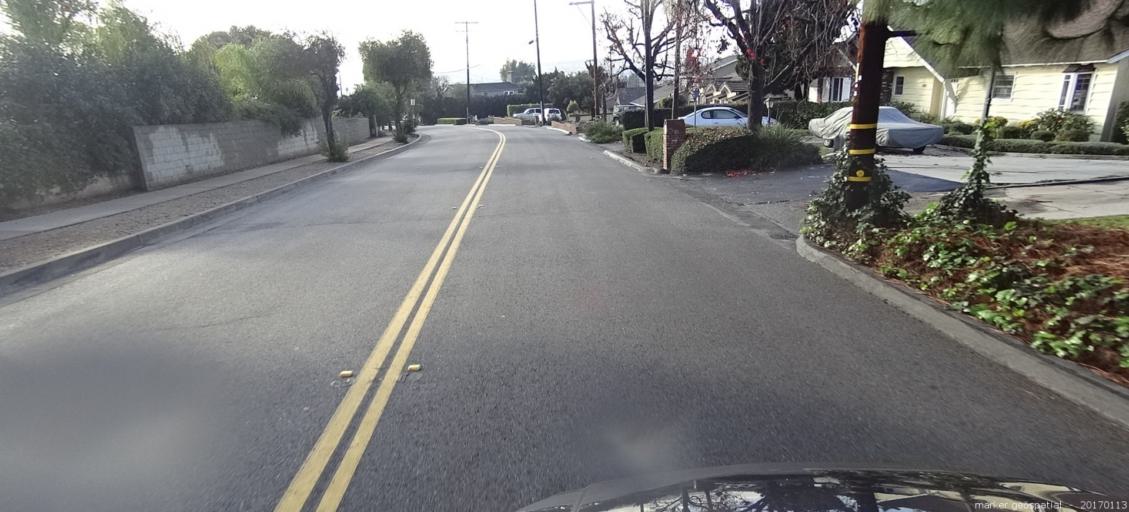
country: US
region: California
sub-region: Orange County
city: La Habra
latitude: 33.9441
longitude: -117.9581
